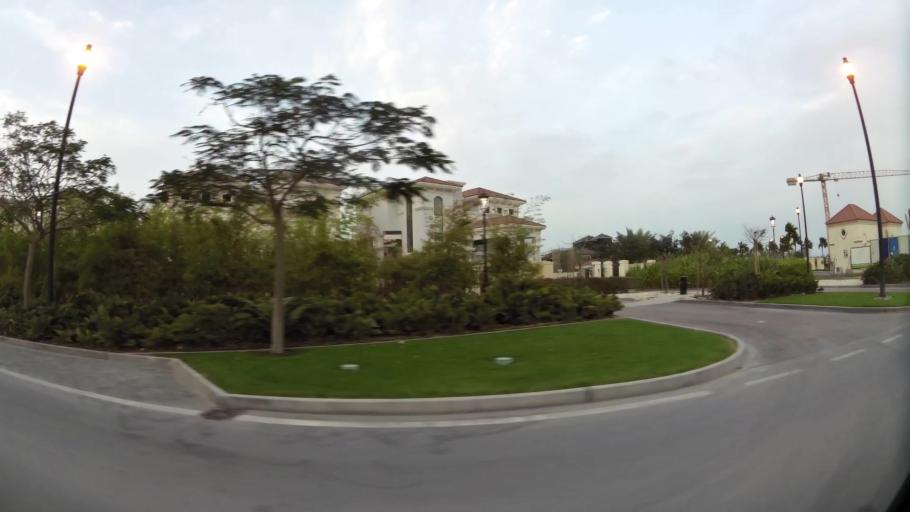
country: QA
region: Baladiyat ad Dawhah
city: Doha
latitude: 25.3619
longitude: 51.5655
